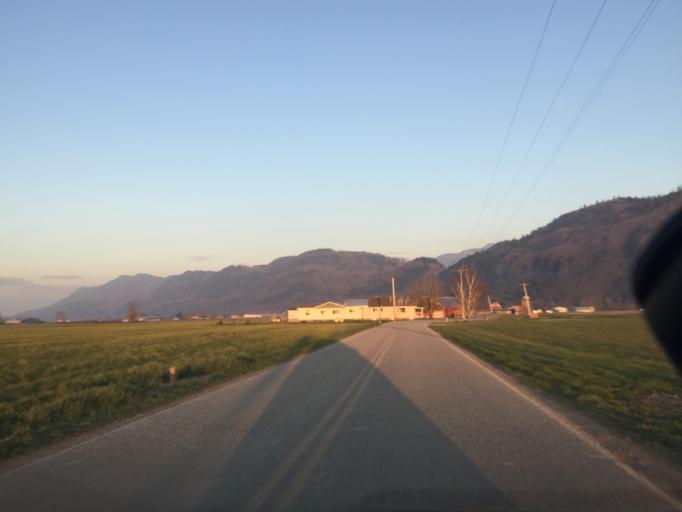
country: US
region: Washington
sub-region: Whatcom County
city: Sumas
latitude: 49.0000
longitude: -122.1969
